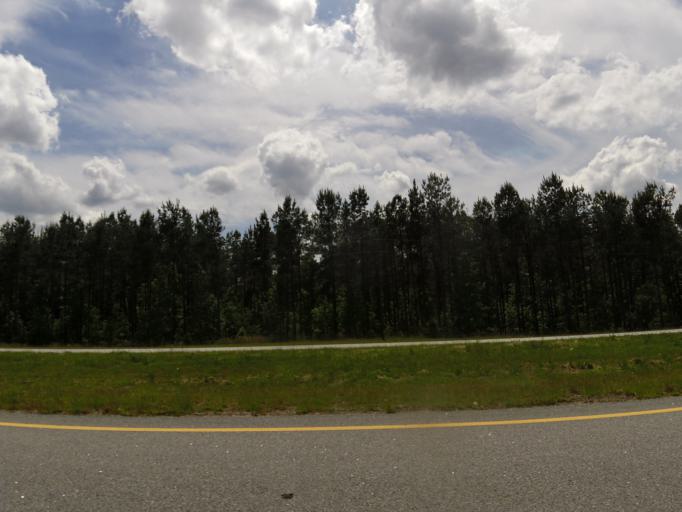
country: US
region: Georgia
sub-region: Jefferson County
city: Wadley
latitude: 32.7789
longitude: -82.3880
